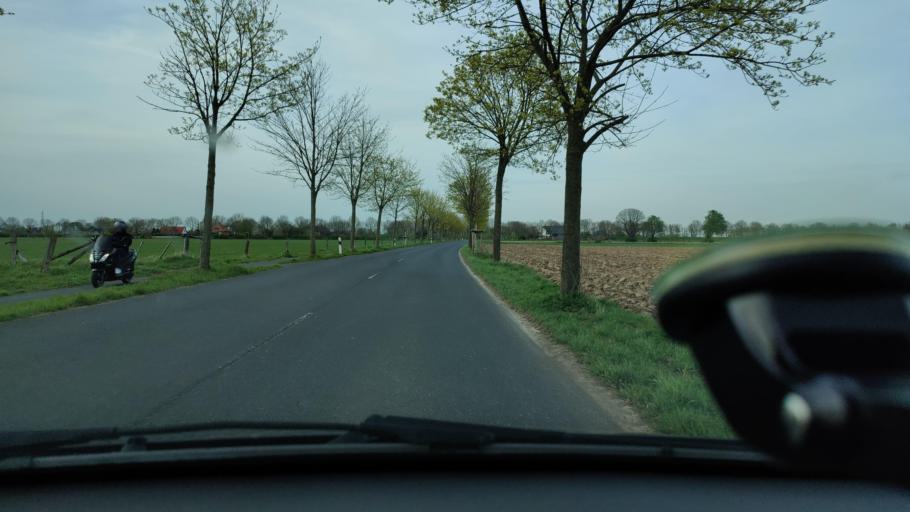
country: DE
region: North Rhine-Westphalia
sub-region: Regierungsbezirk Dusseldorf
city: Kleve
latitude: 51.7861
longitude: 6.1775
